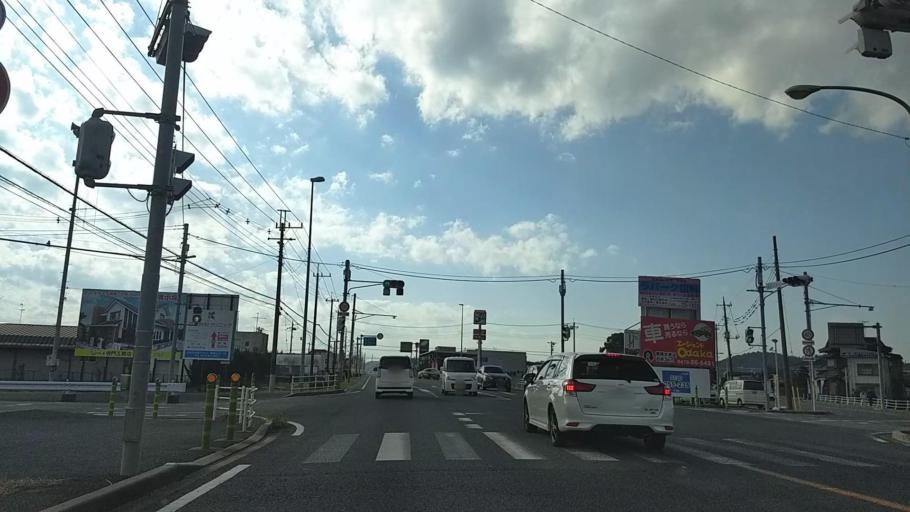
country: JP
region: Chiba
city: Naruto
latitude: 35.6003
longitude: 140.4065
